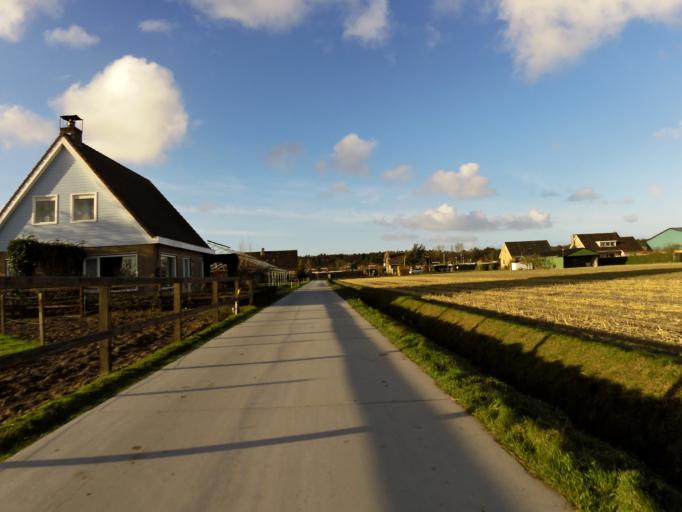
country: NL
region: South Holland
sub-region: Gemeente Noordwijkerhout
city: Noordwijkerhout
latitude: 52.2705
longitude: 4.4787
